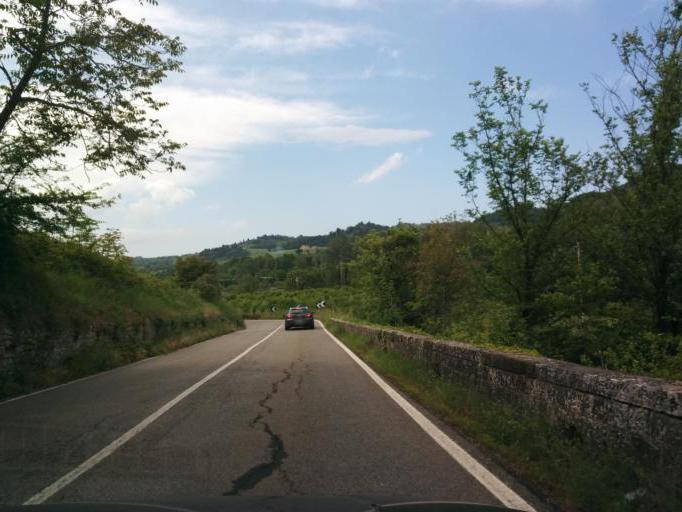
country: IT
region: Tuscany
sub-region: Province of Florence
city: Sambuca
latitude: 43.6072
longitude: 11.1941
